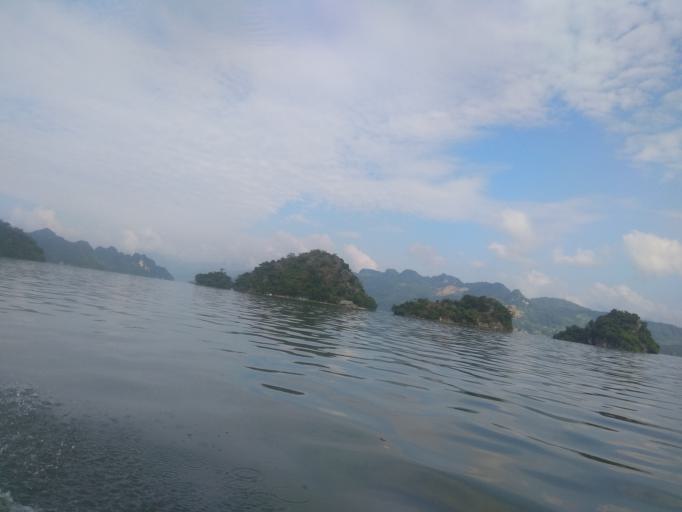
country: VN
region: Hoa Binh
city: Da Bac
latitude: 20.7592
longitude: 105.1575
